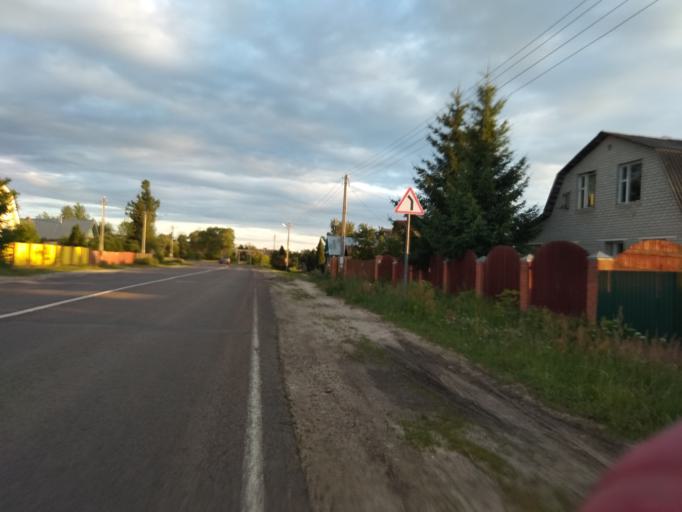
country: RU
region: Moskovskaya
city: Kerva
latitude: 55.5935
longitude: 39.7014
